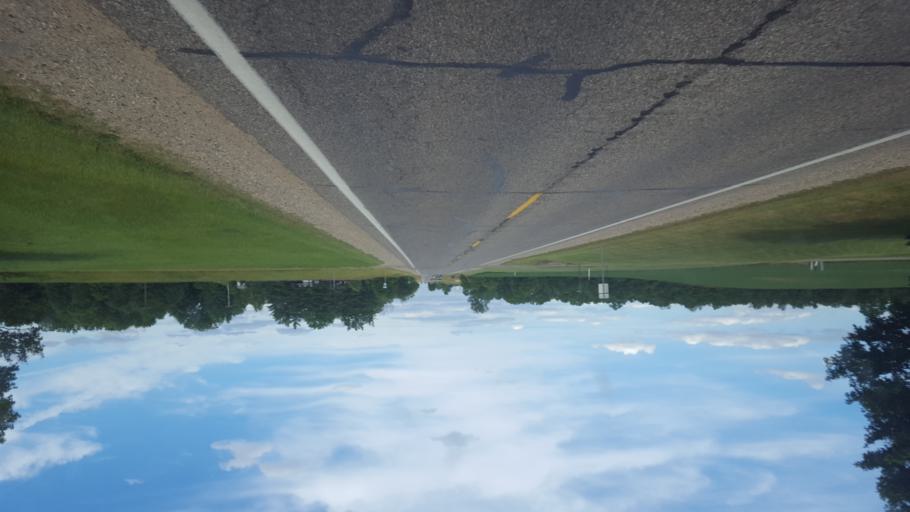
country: US
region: Michigan
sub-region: Eaton County
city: Charlotte
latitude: 42.5678
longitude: -84.9563
